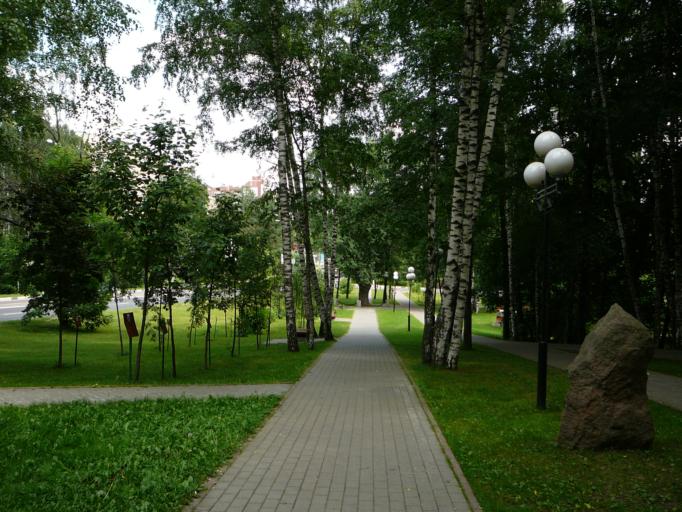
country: RU
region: Moskovskaya
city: Krasnogorsk
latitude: 55.8188
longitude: 37.3270
